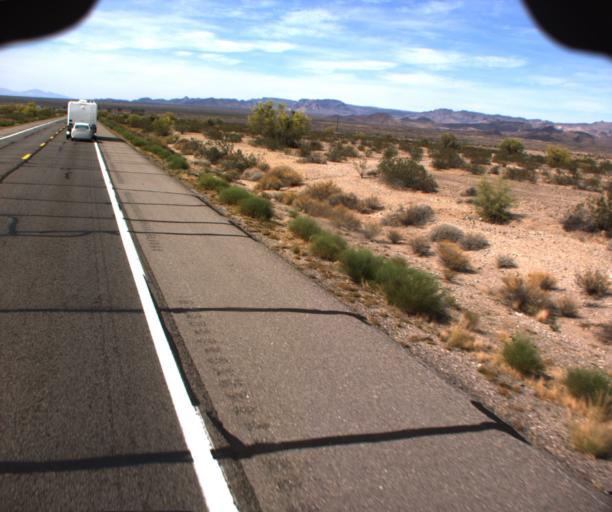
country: US
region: Arizona
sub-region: Mohave County
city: Desert Hills
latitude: 34.7131
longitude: -114.3076
